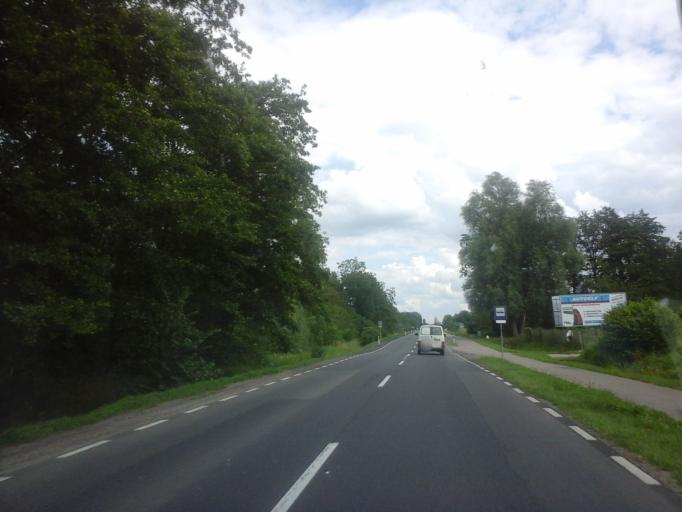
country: PL
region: West Pomeranian Voivodeship
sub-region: Powiat stargardzki
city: Stargard Szczecinski
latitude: 53.3271
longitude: 15.0709
